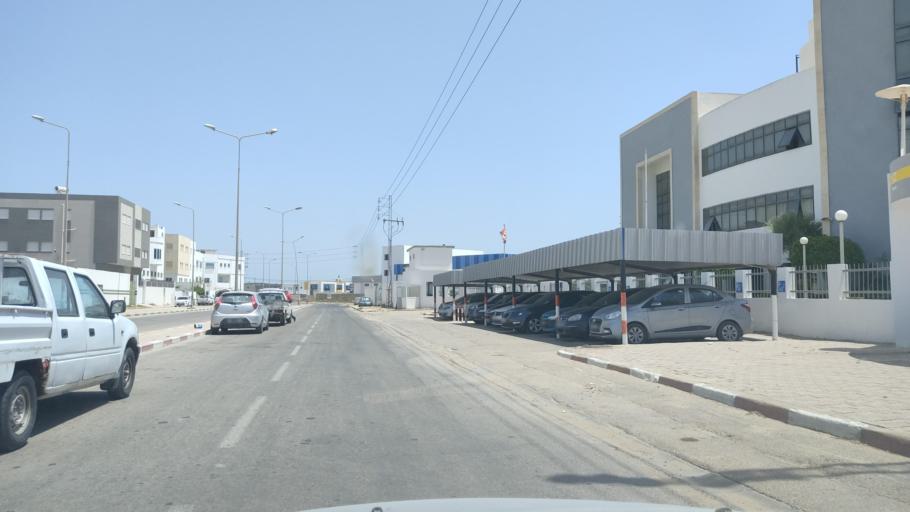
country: TN
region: Safaqis
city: Sfax
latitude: 34.6626
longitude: 10.6951
